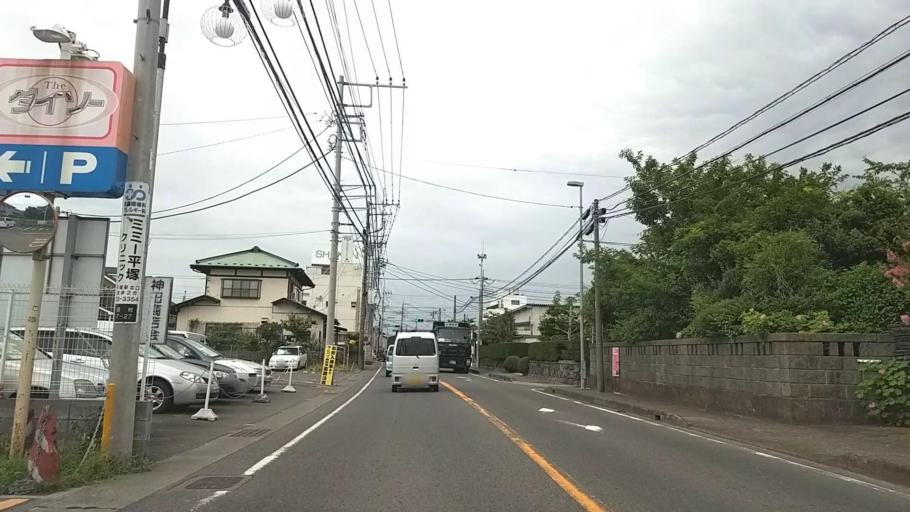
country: JP
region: Kanagawa
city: Hiratsuka
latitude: 35.3746
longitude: 139.3660
